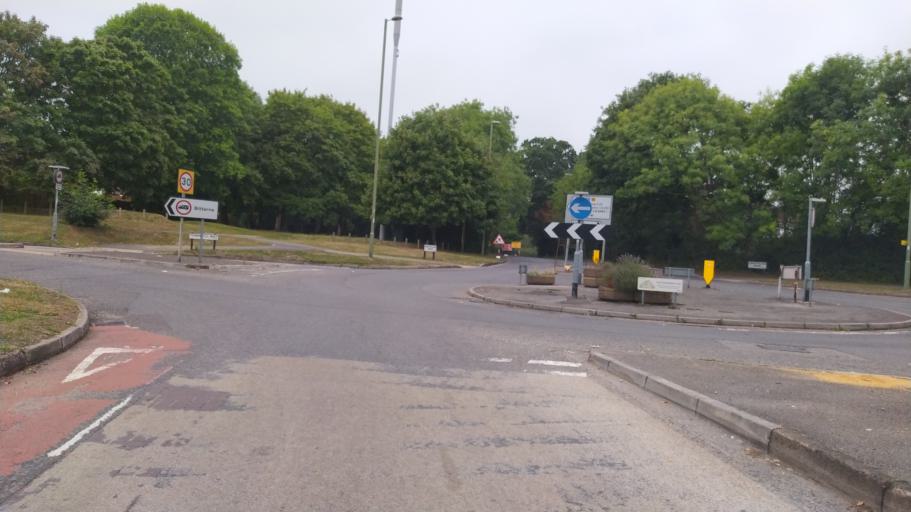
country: GB
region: England
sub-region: Hampshire
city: West End
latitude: 50.9343
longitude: -1.3489
